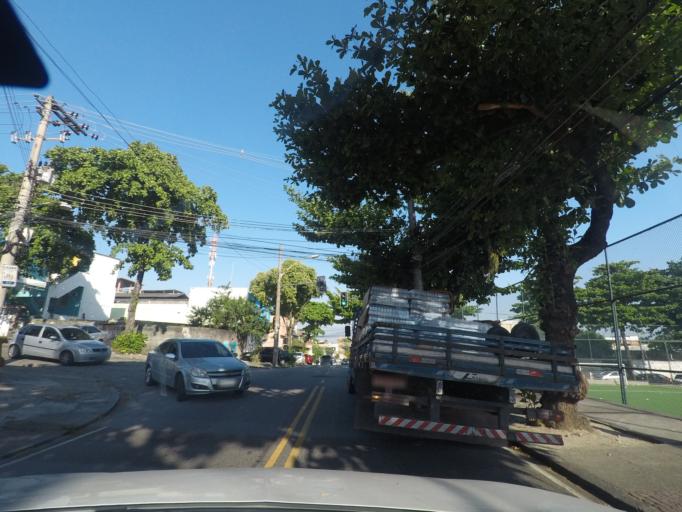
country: BR
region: Rio de Janeiro
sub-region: Duque De Caxias
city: Duque de Caxias
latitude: -22.8304
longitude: -43.2825
